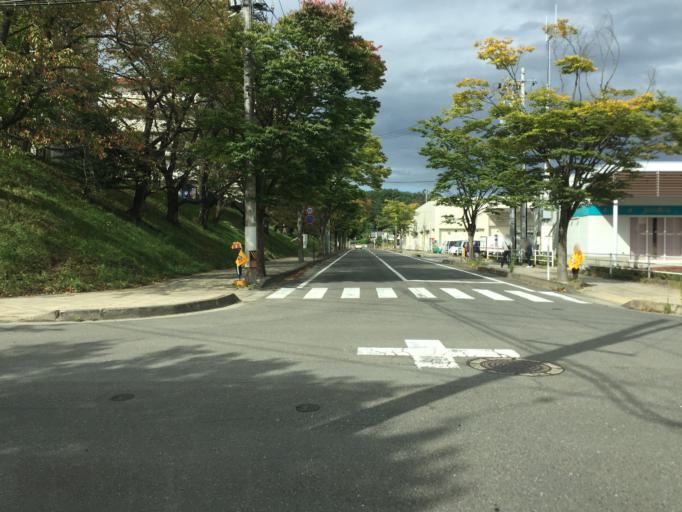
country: JP
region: Fukushima
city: Fukushima-shi
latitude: 37.6971
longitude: 140.4700
